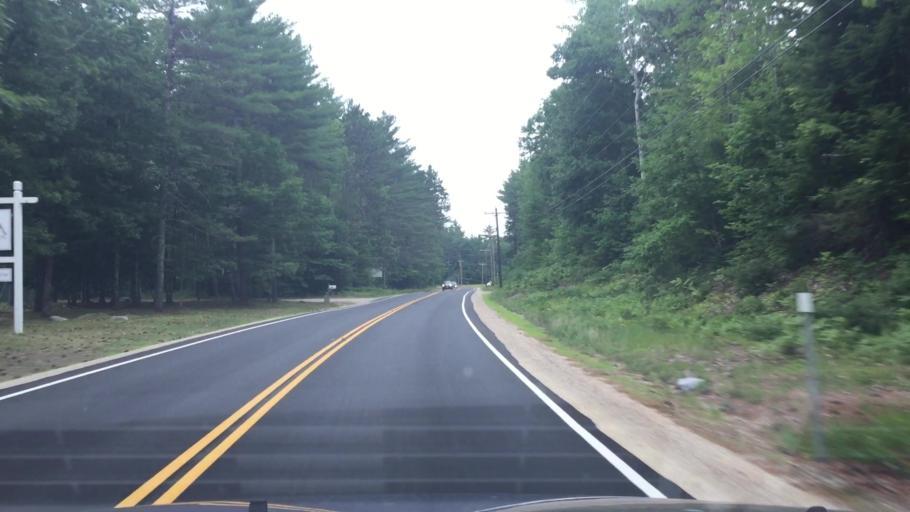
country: US
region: New Hampshire
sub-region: Carroll County
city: Freedom
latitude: 43.8554
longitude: -71.0896
